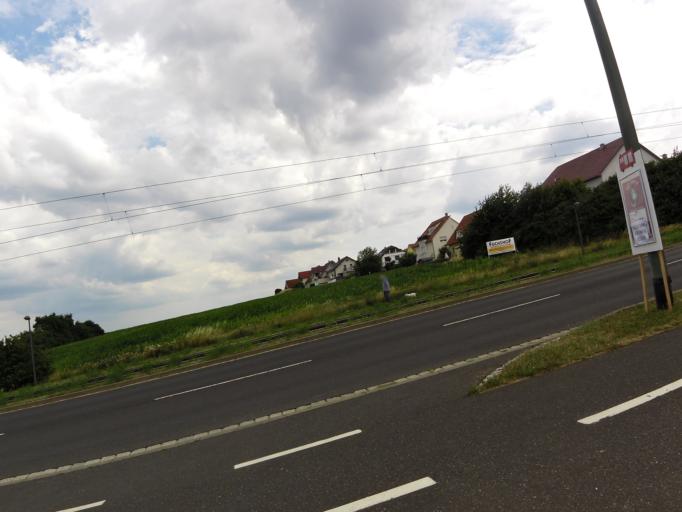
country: DE
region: Bavaria
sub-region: Regierungsbezirk Unterfranken
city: Eibelstadt
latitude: 49.7266
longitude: 9.9671
